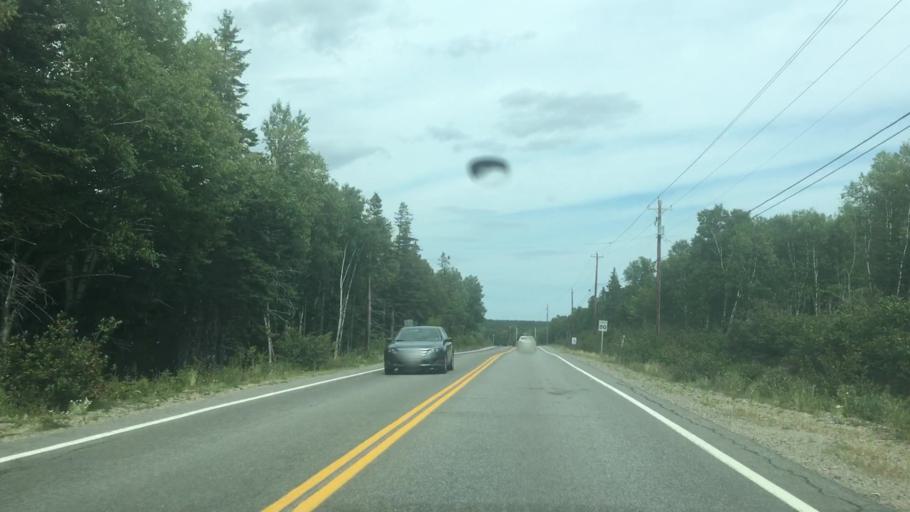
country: CA
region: Nova Scotia
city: Sydney Mines
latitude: 46.5035
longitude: -60.4361
